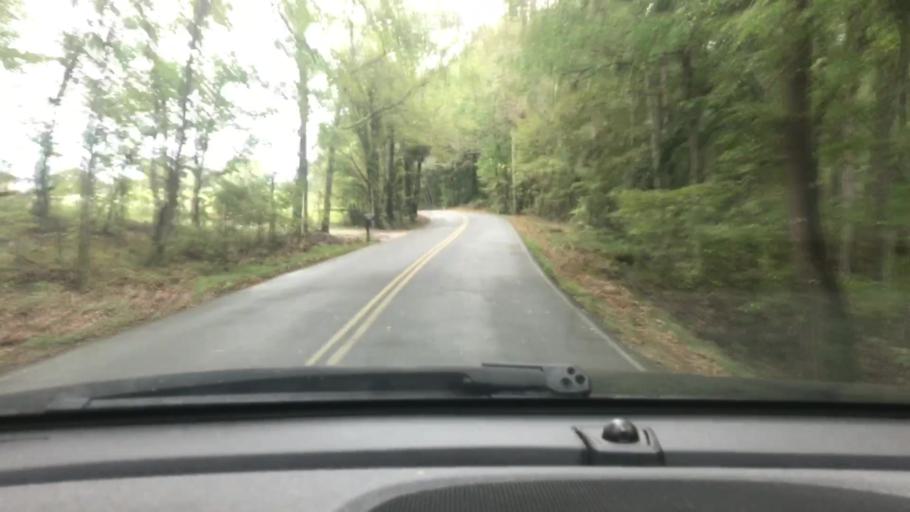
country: US
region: Tennessee
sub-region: Dickson County
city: Charlotte
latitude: 36.1906
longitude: -87.2865
